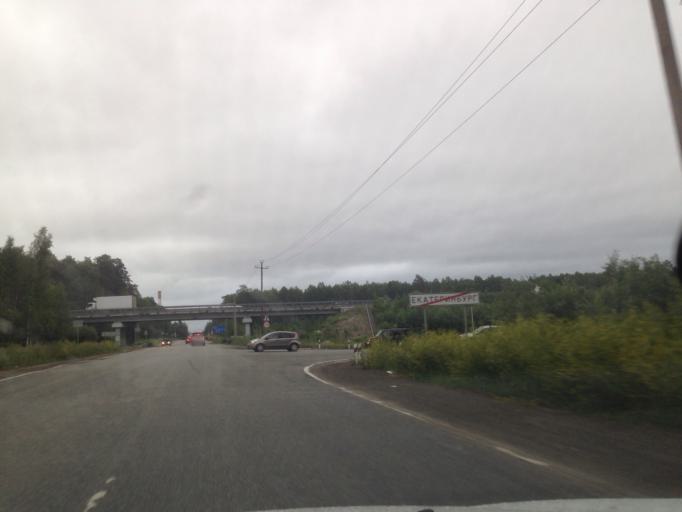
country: RU
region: Sverdlovsk
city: Istok
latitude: 56.8393
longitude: 60.7992
